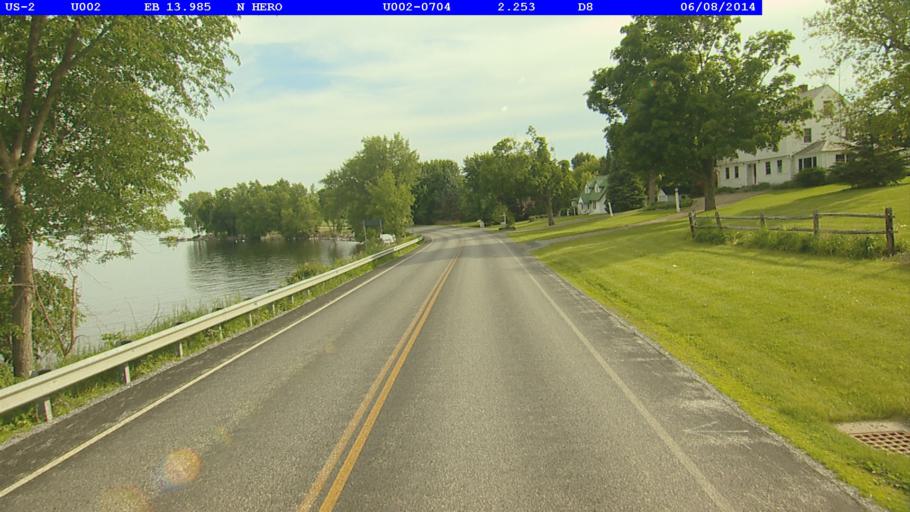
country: US
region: Vermont
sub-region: Grand Isle County
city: North Hero
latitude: 44.8577
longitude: -73.2588
